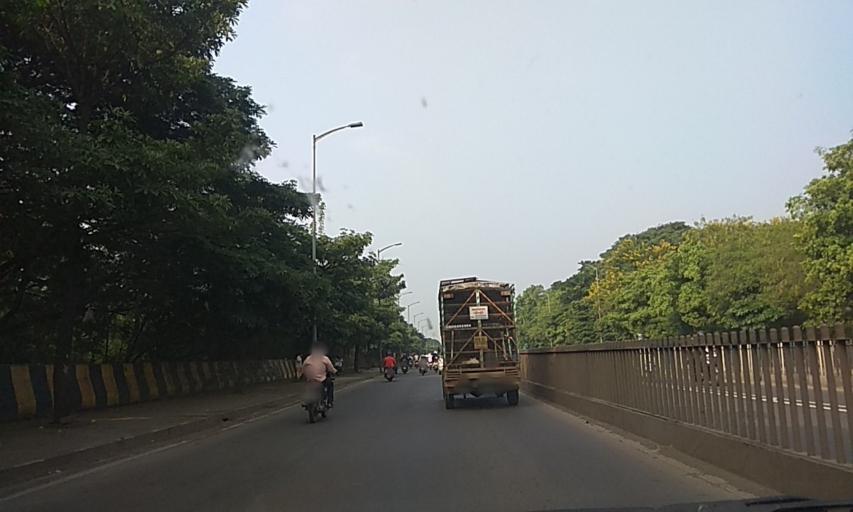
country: IN
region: Maharashtra
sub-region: Pune Division
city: Shivaji Nagar
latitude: 18.5426
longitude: 73.8742
